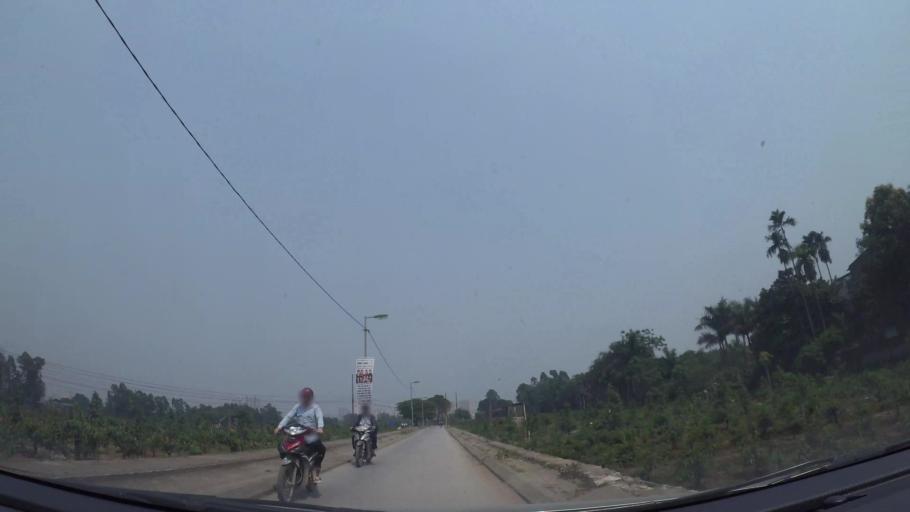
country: VN
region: Ha Noi
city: Ha Dong
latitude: 20.9948
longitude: 105.7629
